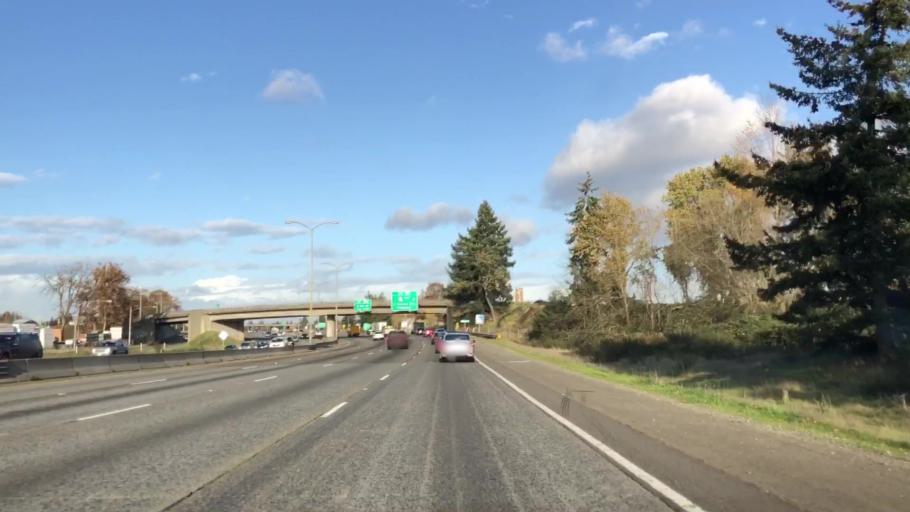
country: US
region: Washington
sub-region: Pierce County
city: McChord Air Force Base
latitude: 47.1581
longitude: -122.4852
